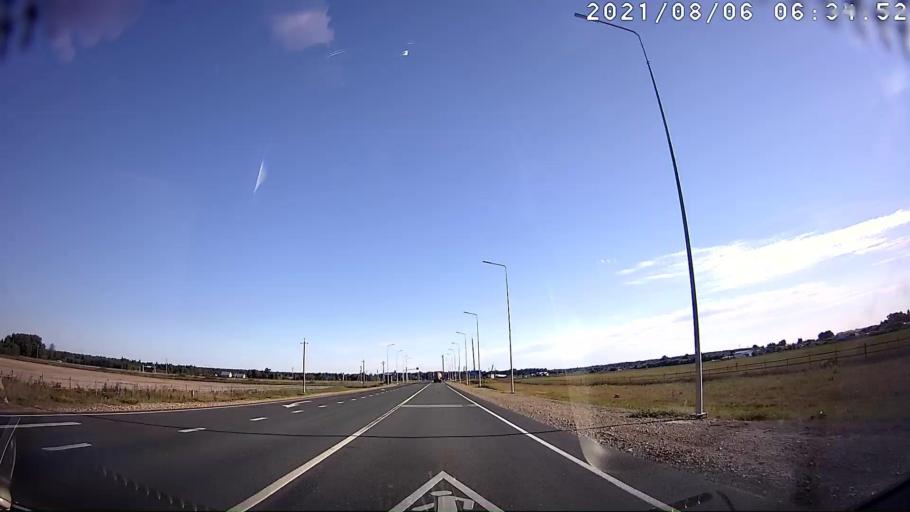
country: RU
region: Mariy-El
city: Suslonger
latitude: 56.2122
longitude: 48.2364
